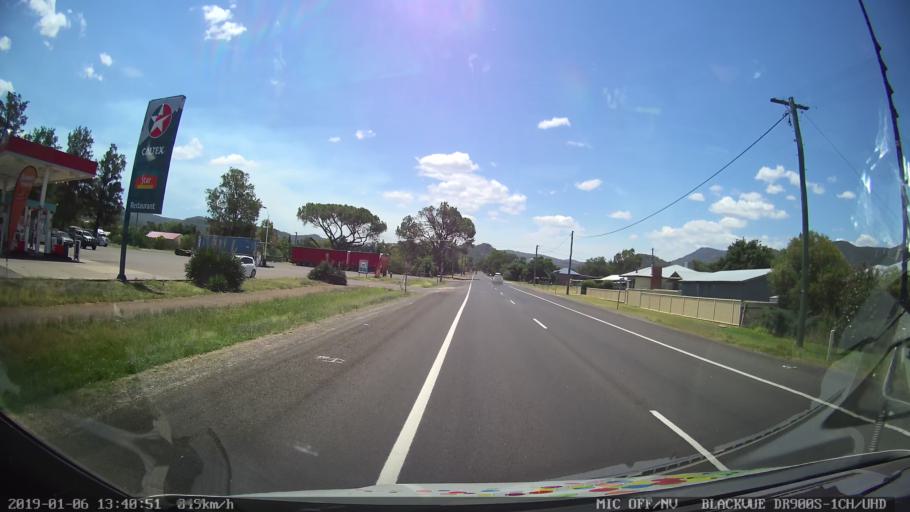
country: AU
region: New South Wales
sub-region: Tamworth Municipality
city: Kootingal
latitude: -31.0230
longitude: 151.0695
